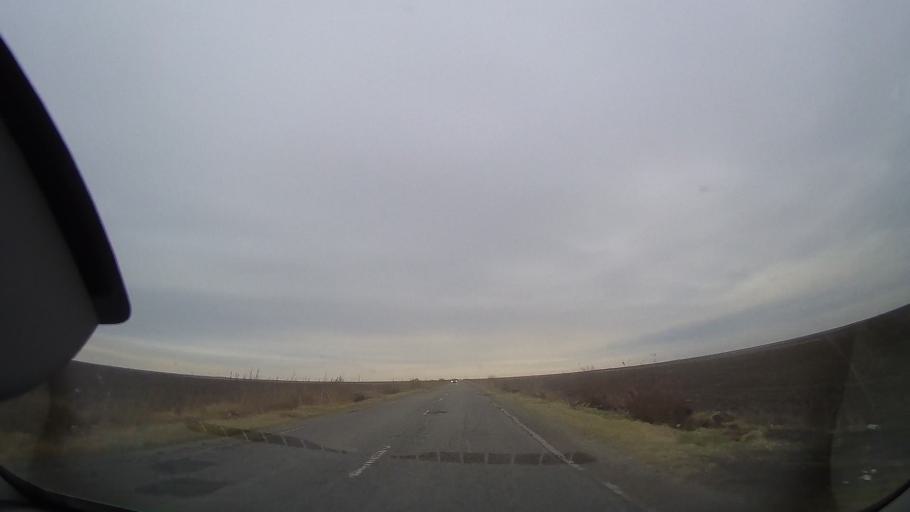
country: RO
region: Ialomita
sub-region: Oras Amara
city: Amara
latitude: 44.6541
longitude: 27.3006
